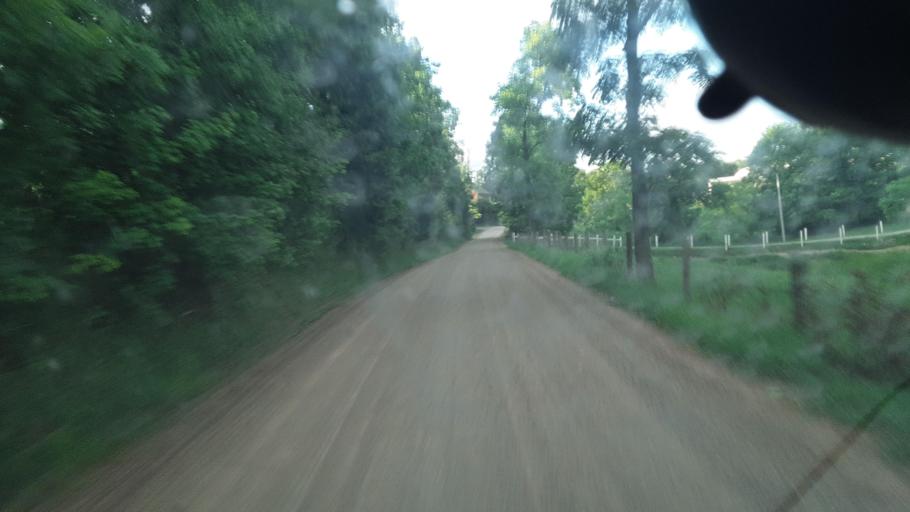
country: US
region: Ohio
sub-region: Holmes County
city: Millersburg
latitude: 40.4317
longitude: -81.8484
